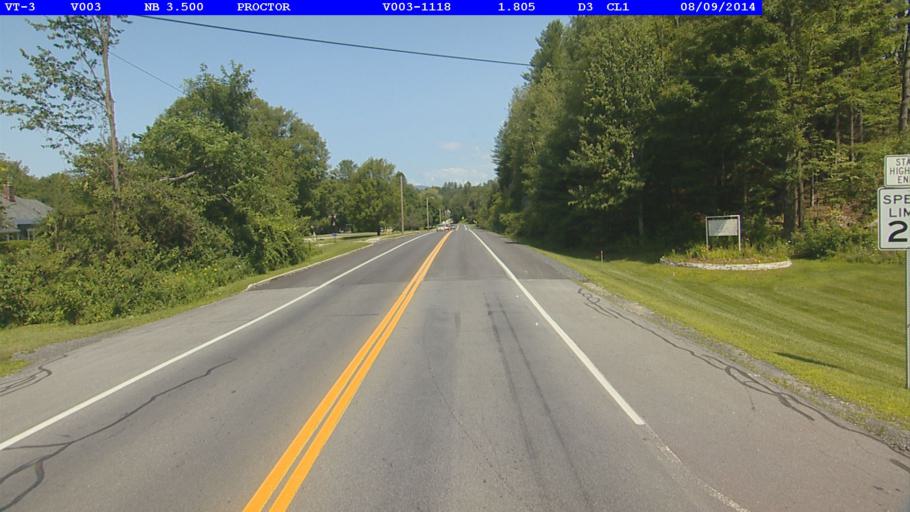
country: US
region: Vermont
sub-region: Rutland County
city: West Rutland
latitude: 43.6498
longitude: -73.0328
